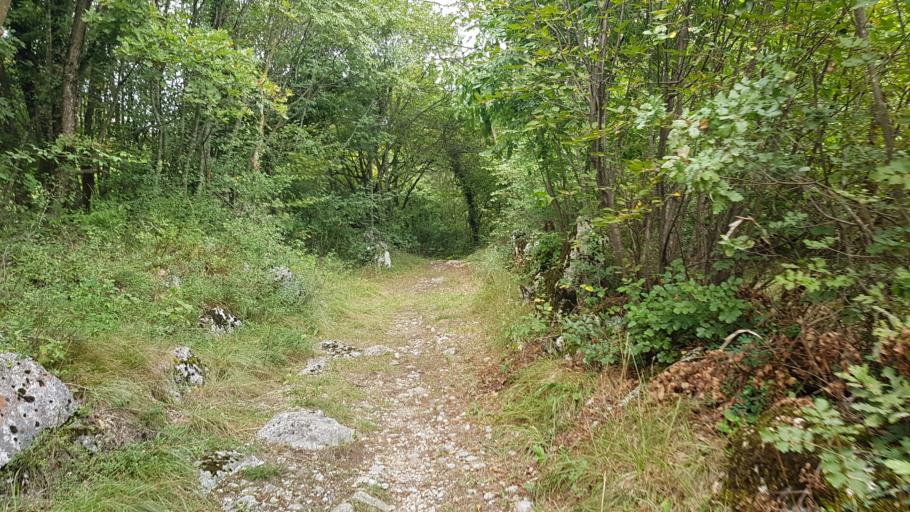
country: IT
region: Trentino-Alto Adige
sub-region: Provincia di Trento
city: Cavedine
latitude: 46.0076
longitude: 10.9764
